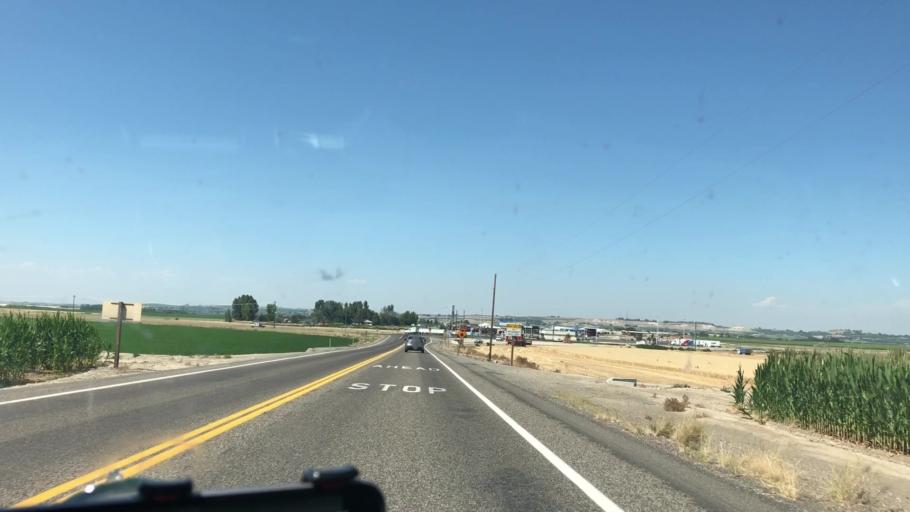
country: US
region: Idaho
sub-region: Owyhee County
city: Marsing
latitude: 43.5417
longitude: -116.8517
